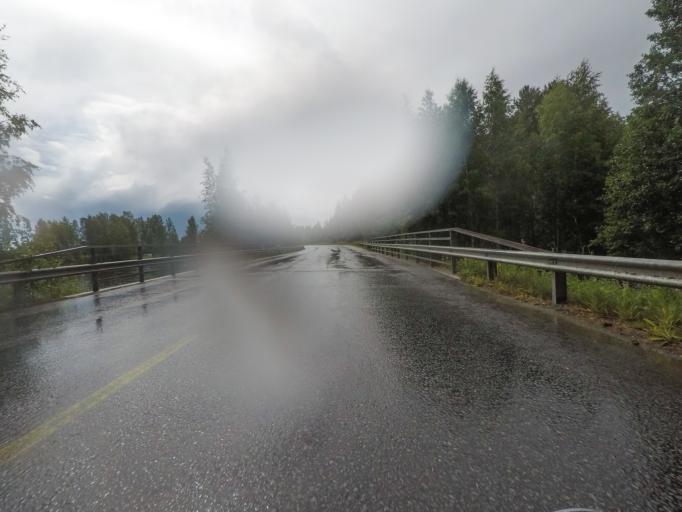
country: FI
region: Central Finland
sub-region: Jyvaeskylae
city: Toivakka
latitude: 62.1468
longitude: 26.1224
